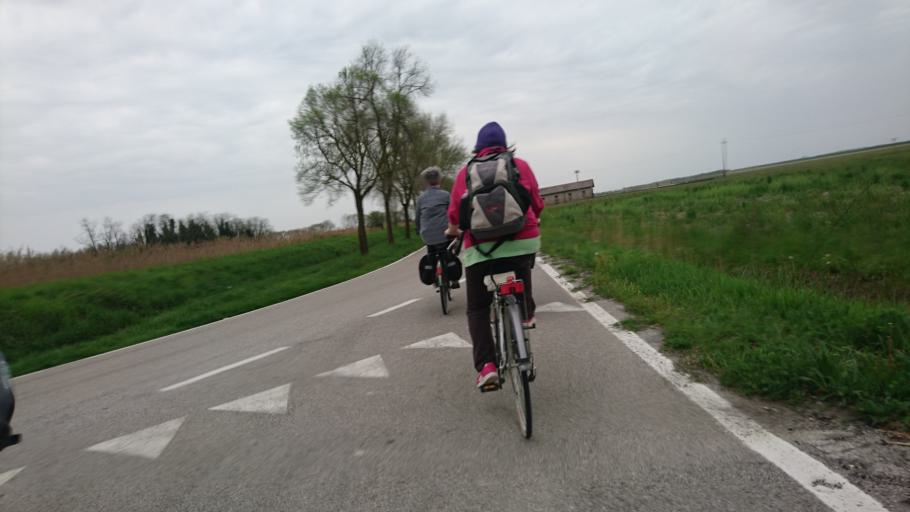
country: IT
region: Veneto
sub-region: Provincia di Venezia
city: Cesarolo
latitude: 45.6838
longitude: 12.9924
